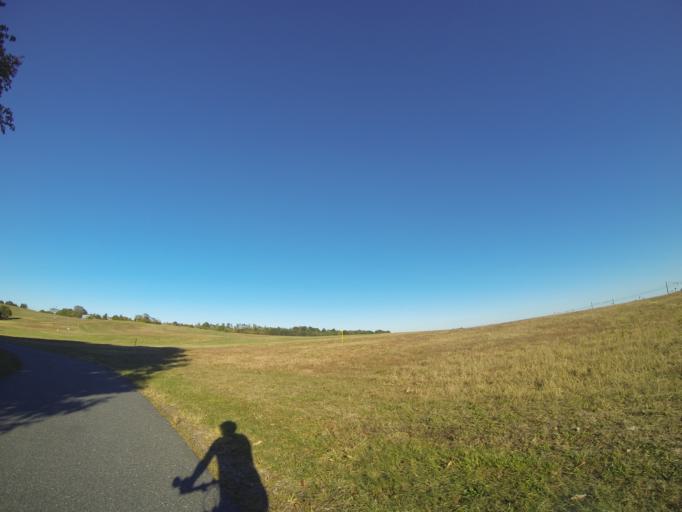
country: US
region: Maryland
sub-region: Anne Arundel County
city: Linthicum
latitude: 39.1919
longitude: -76.6708
